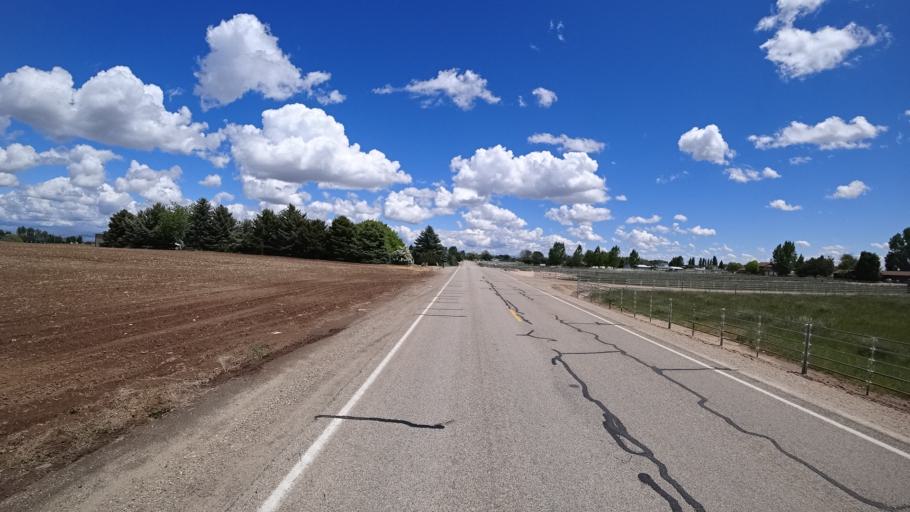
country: US
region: Idaho
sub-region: Ada County
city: Meridian
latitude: 43.5830
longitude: -116.4405
